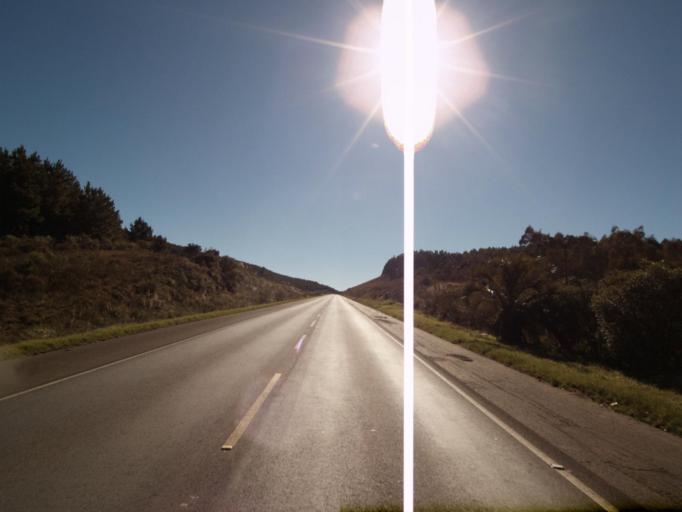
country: BR
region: Parana
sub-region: Palmas
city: Palmas
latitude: -26.6709
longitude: -51.5499
